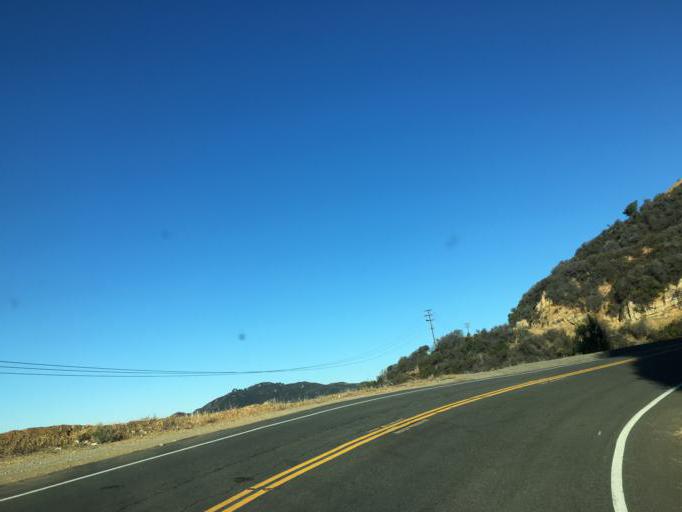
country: US
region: California
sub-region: Los Angeles County
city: Agoura Hills
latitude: 34.0854
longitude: -118.8026
